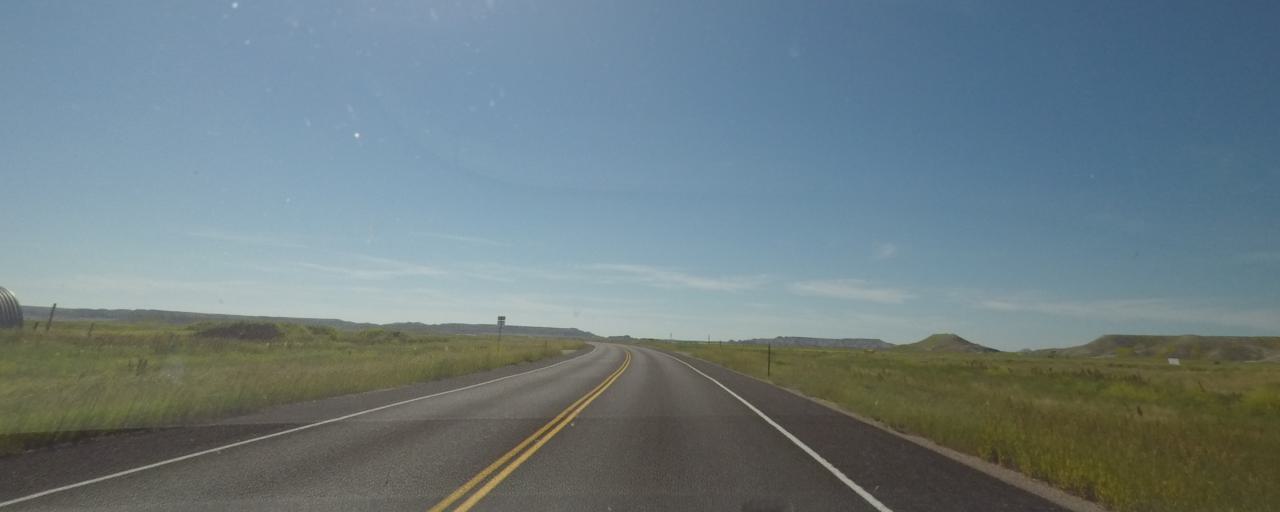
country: US
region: South Dakota
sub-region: Shannon County
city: Porcupine
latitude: 43.7812
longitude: -102.5514
